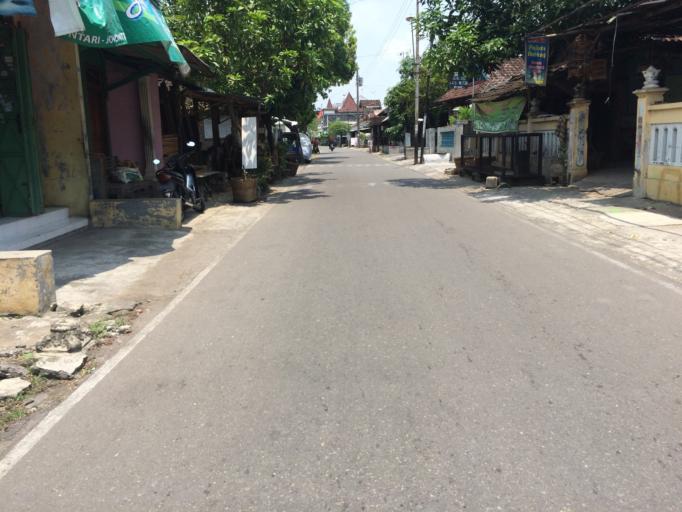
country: ID
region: Central Java
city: Grogol
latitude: -7.5921
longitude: 110.8176
